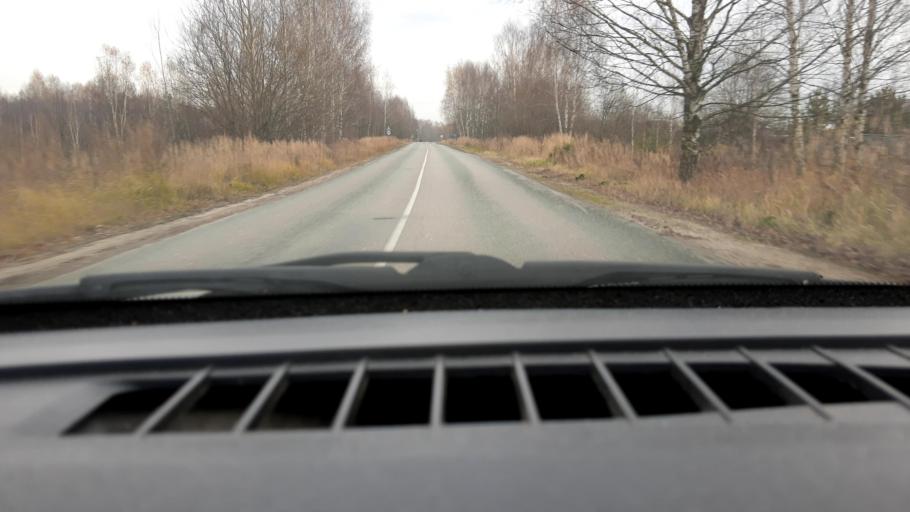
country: RU
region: Nizjnij Novgorod
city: Neklyudovo
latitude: 56.4362
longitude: 43.9210
